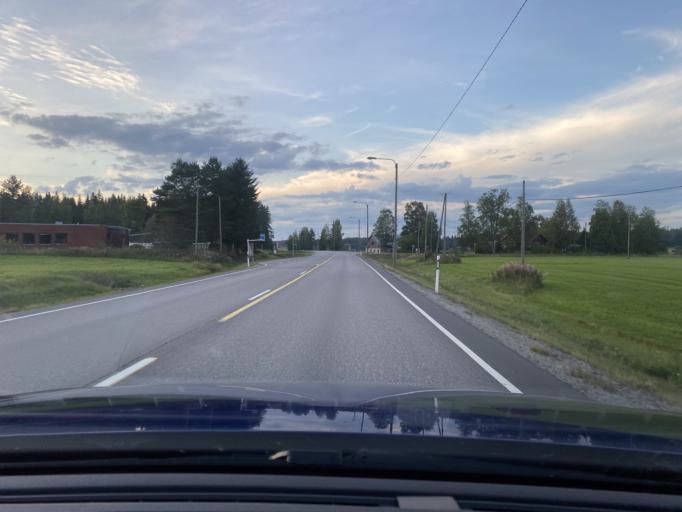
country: FI
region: Satakunta
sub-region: Pohjois-Satakunta
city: Kankaanpaeae
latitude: 61.7416
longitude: 22.5250
